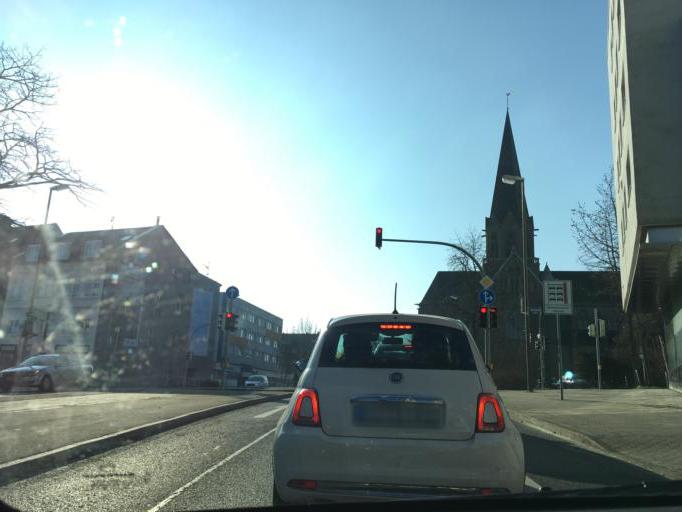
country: DE
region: North Rhine-Westphalia
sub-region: Regierungsbezirk Arnsberg
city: Dortmund
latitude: 51.4898
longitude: 7.5033
